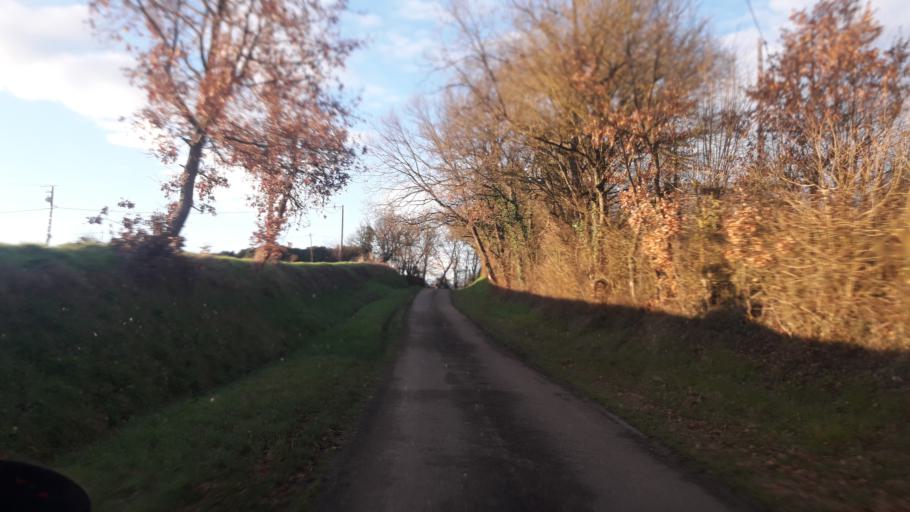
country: FR
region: Midi-Pyrenees
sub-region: Departement du Gers
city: Gimont
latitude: 43.6936
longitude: 0.9258
